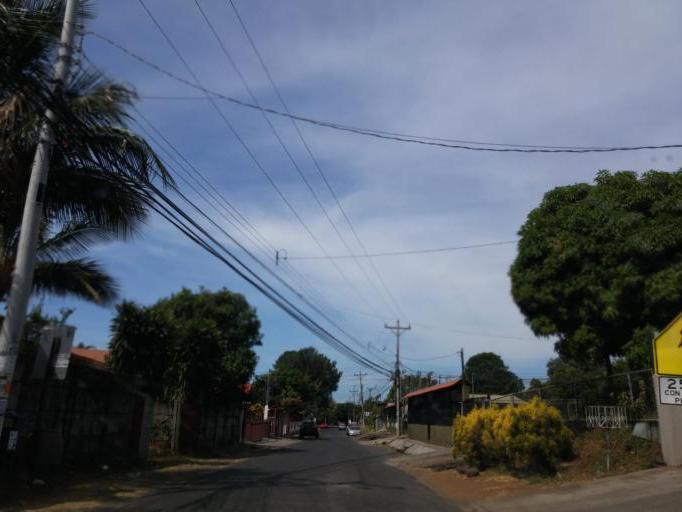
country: CR
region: Alajuela
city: Sabanilla
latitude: 10.0502
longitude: -84.2171
